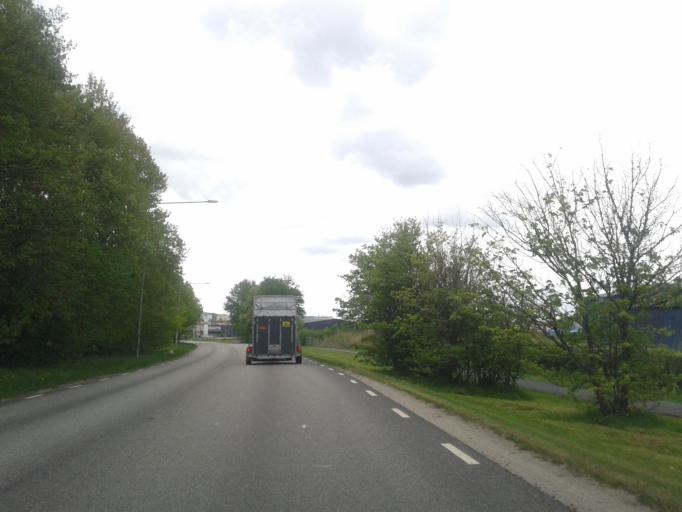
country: SE
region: Vaestra Goetaland
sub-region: Kungalvs Kommun
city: Kungalv
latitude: 57.8835
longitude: 11.9876
